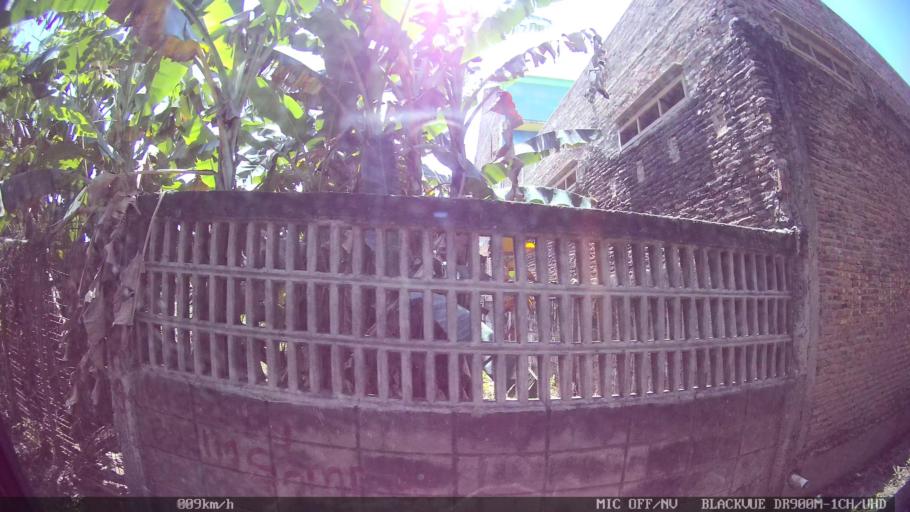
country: ID
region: Lampung
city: Kedaton
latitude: -5.3792
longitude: 105.2923
